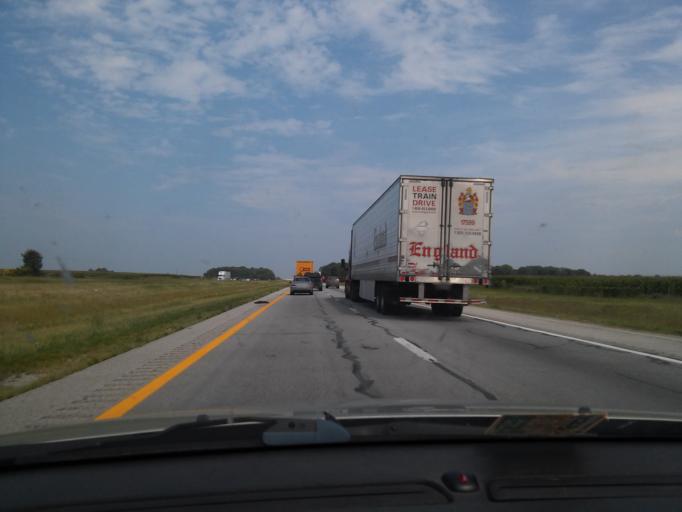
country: US
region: Ohio
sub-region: Preble County
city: Lewisburg
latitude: 39.8378
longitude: -84.4804
